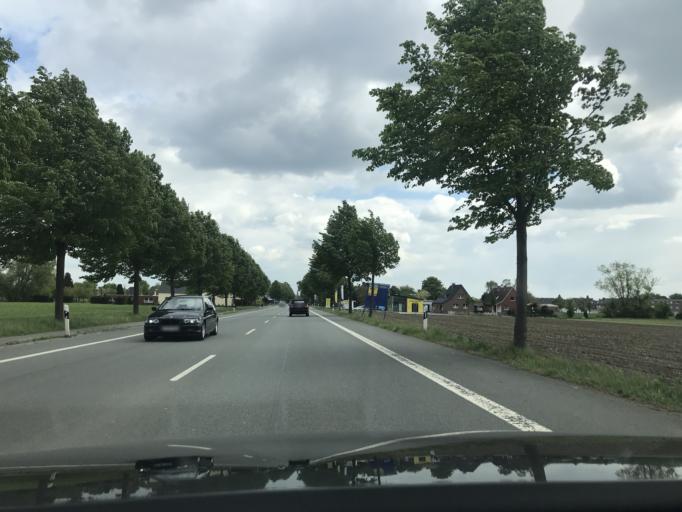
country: DE
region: North Rhine-Westphalia
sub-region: Regierungsbezirk Detmold
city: Rheda-Wiedenbruck
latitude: 51.8639
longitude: 8.2706
